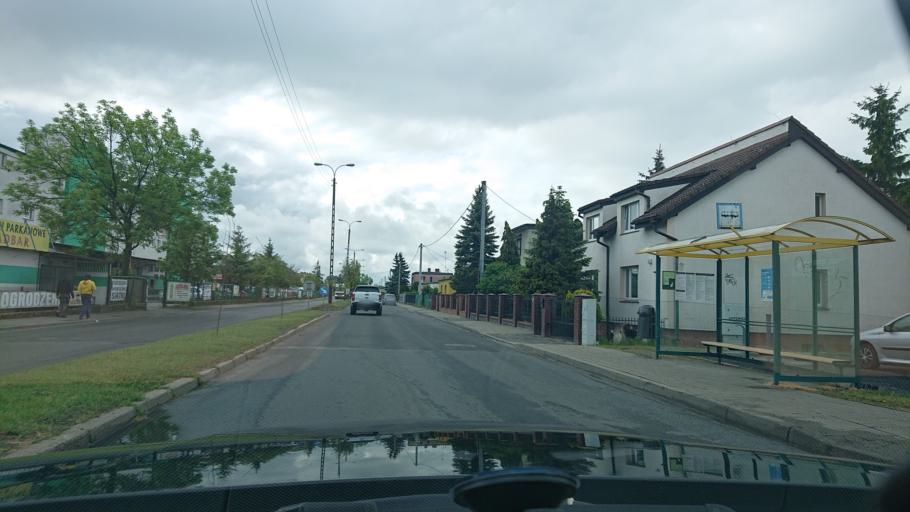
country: PL
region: Greater Poland Voivodeship
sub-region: Powiat gnieznienski
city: Gniezno
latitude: 52.5404
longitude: 17.6250
